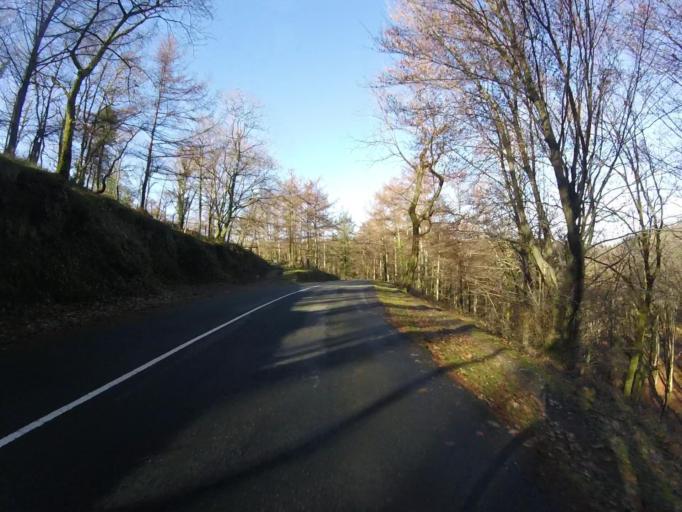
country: ES
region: Basque Country
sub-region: Provincia de Guipuzcoa
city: Irun
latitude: 43.2925
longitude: -1.7789
